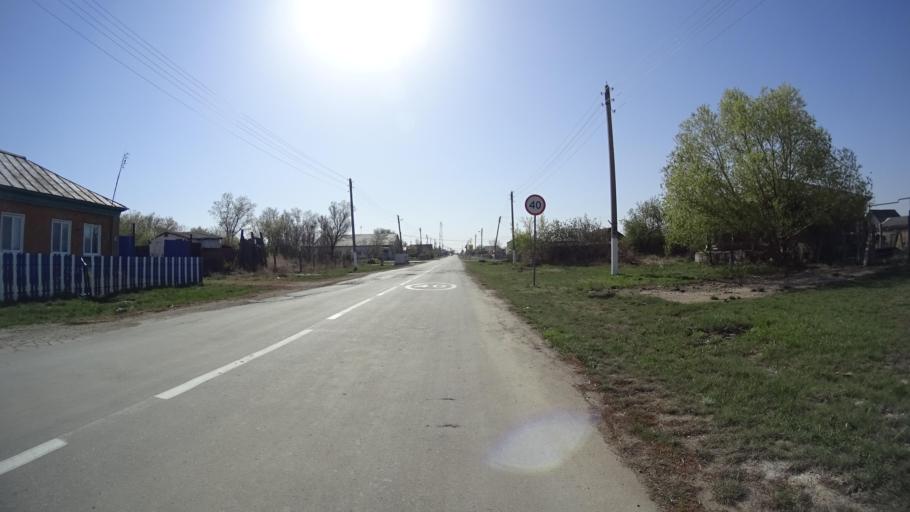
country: RU
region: Chelyabinsk
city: Chesma
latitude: 53.7969
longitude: 61.0276
